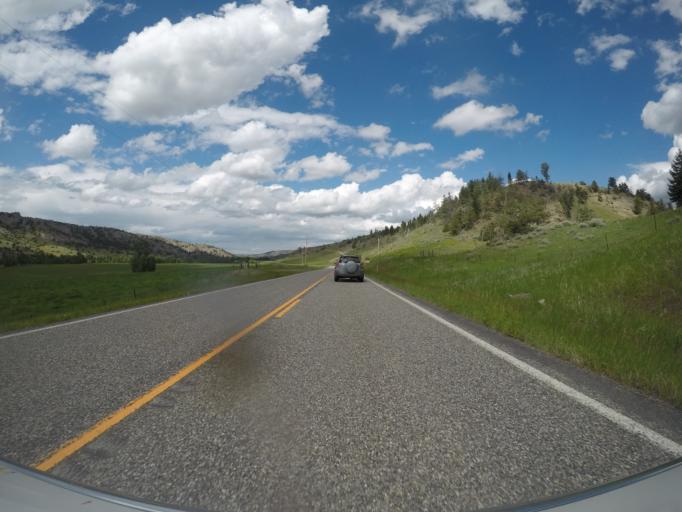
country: US
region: Montana
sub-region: Sweet Grass County
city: Big Timber
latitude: 45.7030
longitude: -110.0148
